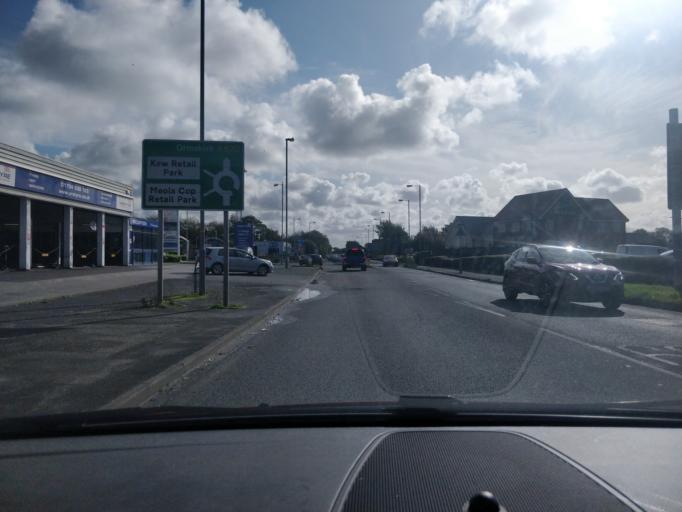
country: GB
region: England
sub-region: Sefton
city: Southport
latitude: 53.6326
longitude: -2.9691
